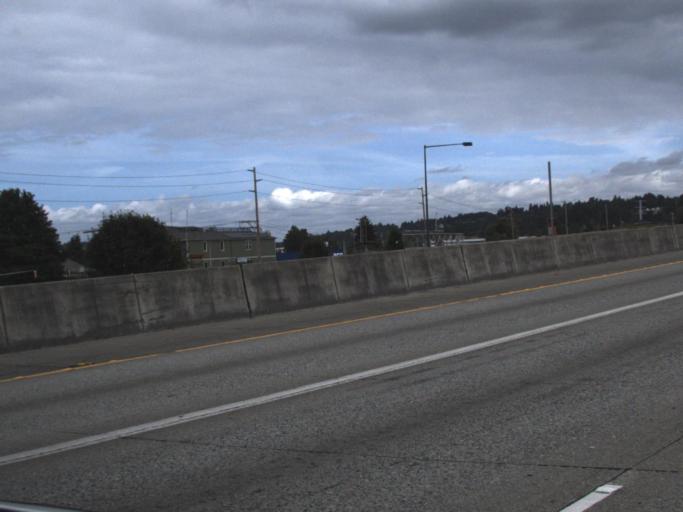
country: US
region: Washington
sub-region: King County
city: Renton
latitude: 47.4831
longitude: -122.1972
